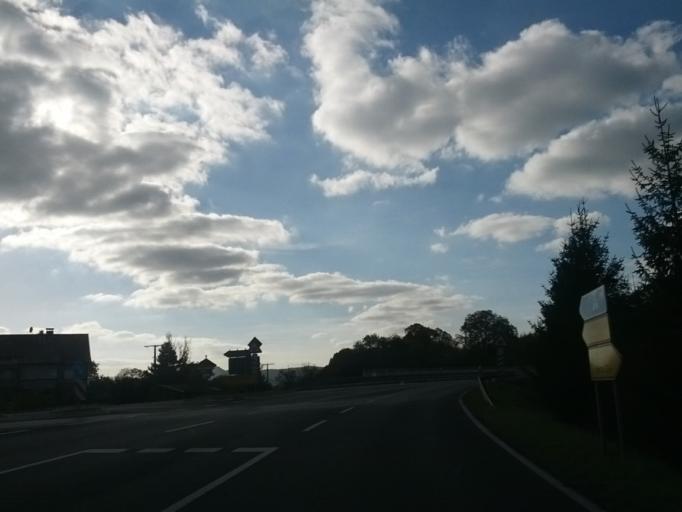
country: DE
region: Thuringia
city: Gerstungen
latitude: 50.9417
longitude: 10.0664
